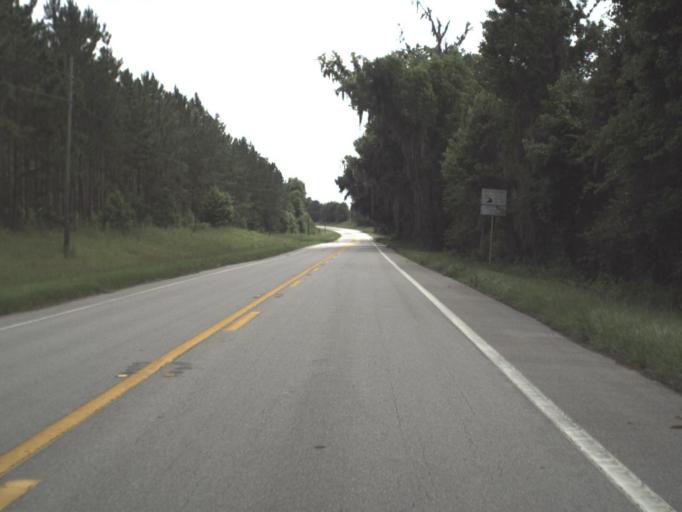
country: US
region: Florida
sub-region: Madison County
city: Madison
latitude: 30.6250
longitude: -83.4394
